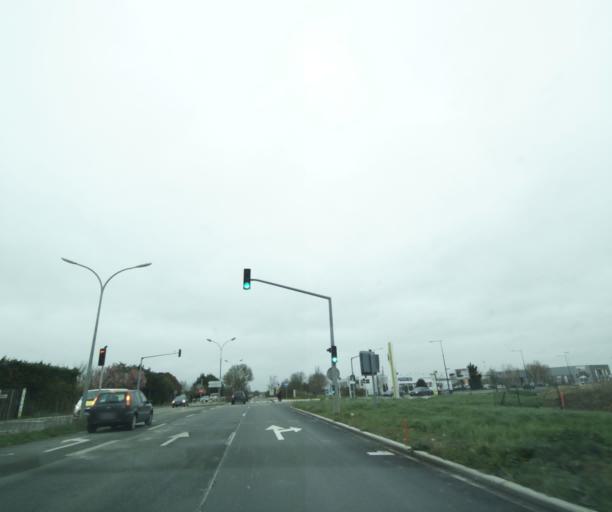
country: FR
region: Poitou-Charentes
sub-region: Departement de la Charente-Maritime
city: Lagord
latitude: 46.1858
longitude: -1.1512
